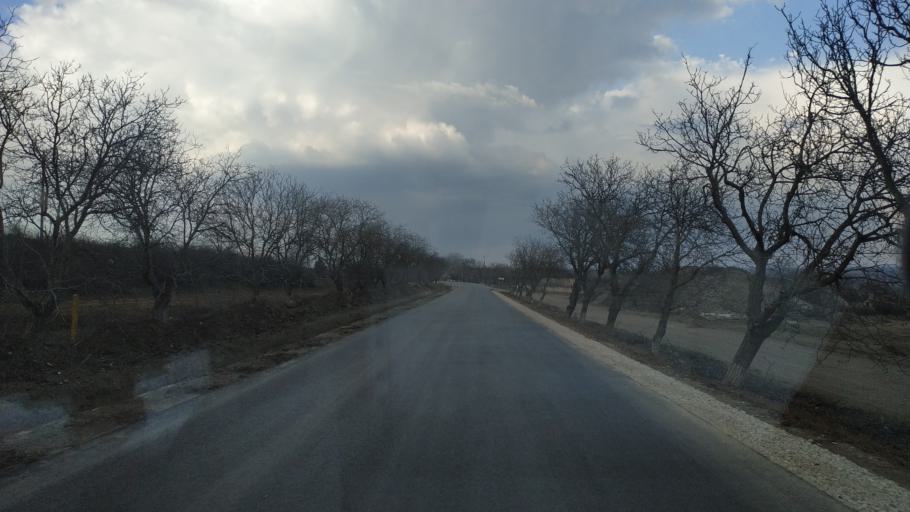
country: MD
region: Anenii Noi
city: Anenii Noi
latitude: 46.9992
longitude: 29.2869
